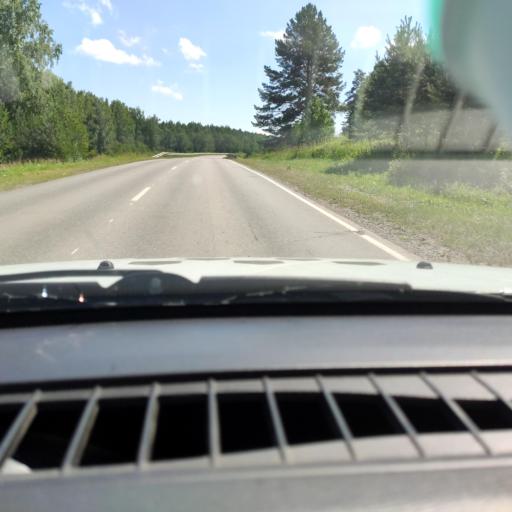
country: RU
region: Bashkortostan
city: Mesyagutovo
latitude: 55.5111
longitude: 58.3147
